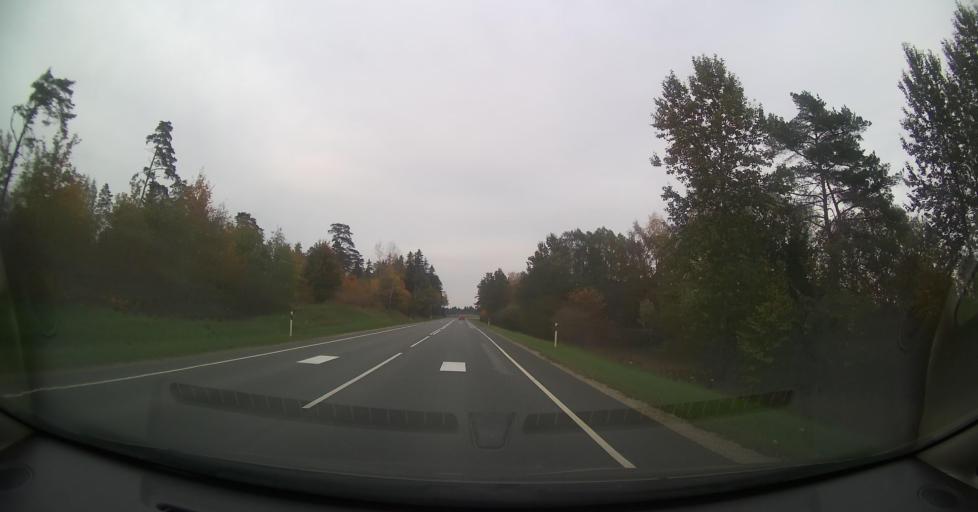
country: EE
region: Harju
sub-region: Nissi vald
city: Turba
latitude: 59.0005
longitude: 24.1098
